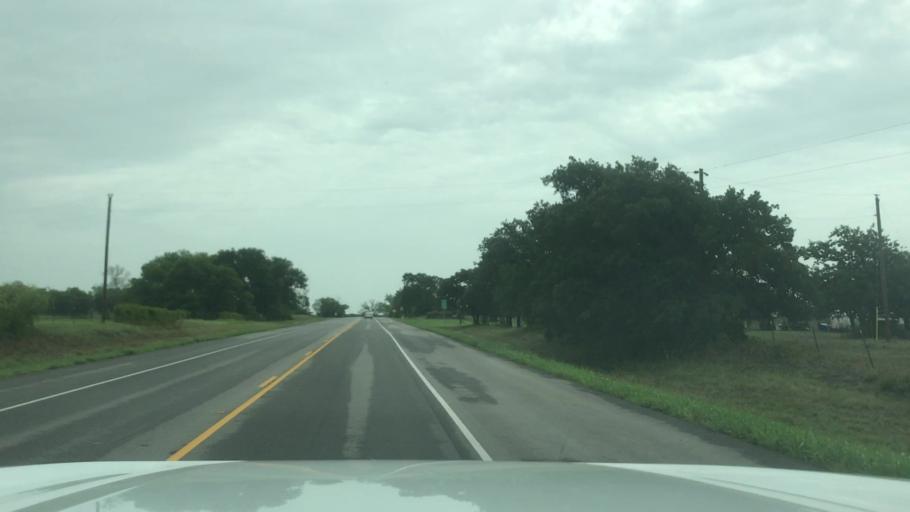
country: US
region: Texas
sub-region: Eastland County
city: Gorman
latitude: 32.2219
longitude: -98.6880
